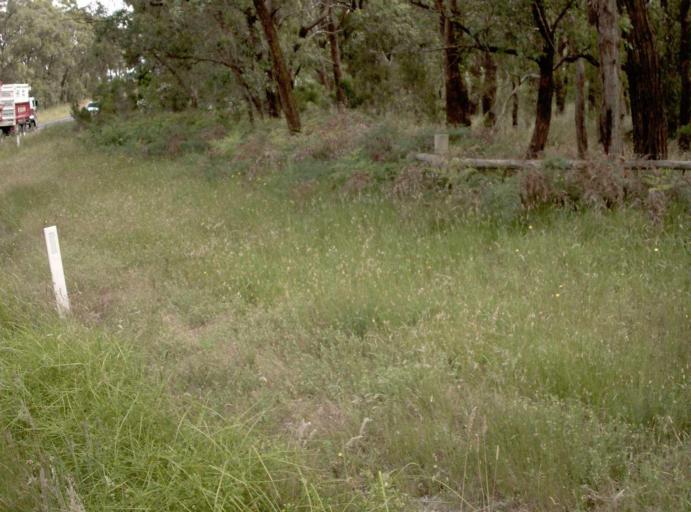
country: AU
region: Victoria
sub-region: Latrobe
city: Moe
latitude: -38.0915
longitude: 146.1991
